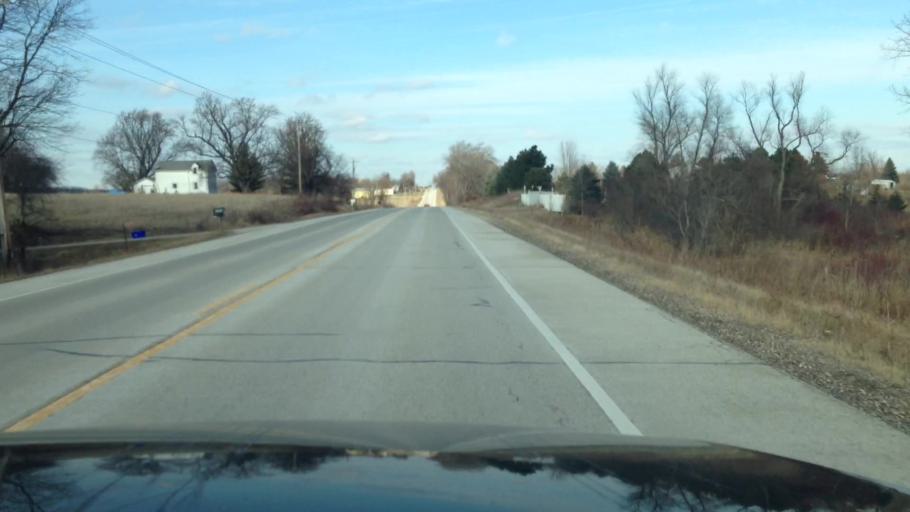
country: US
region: Wisconsin
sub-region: Walworth County
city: East Troy
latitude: 42.7053
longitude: -88.4051
